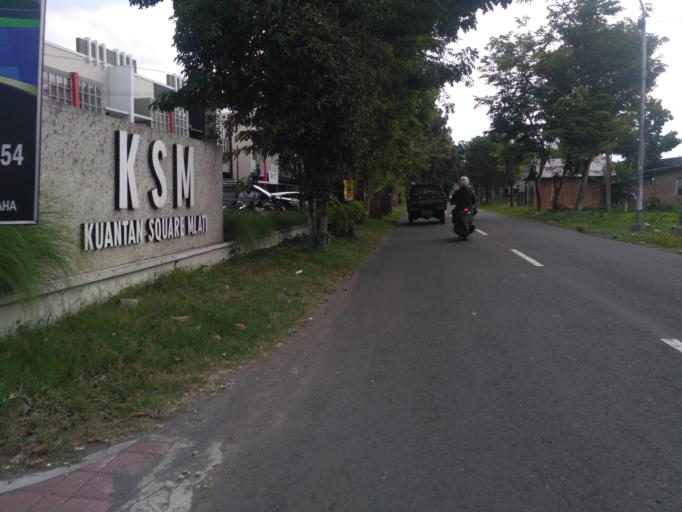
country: ID
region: Daerah Istimewa Yogyakarta
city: Melati
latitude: -7.7404
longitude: 110.3587
